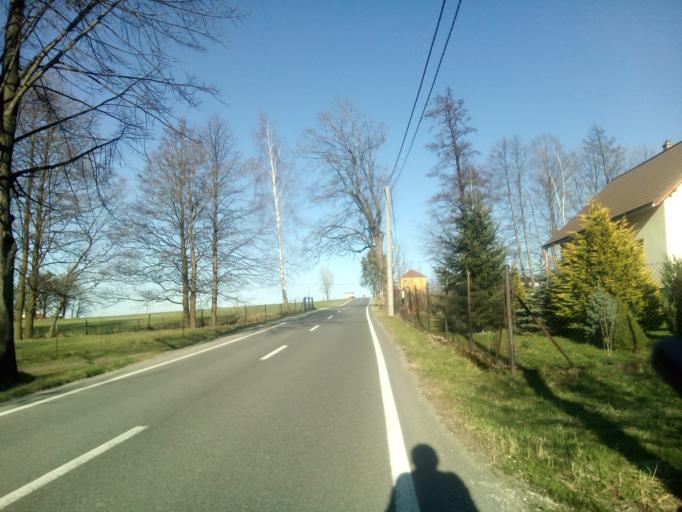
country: CZ
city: Raskovice
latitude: 49.6452
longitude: 18.4710
